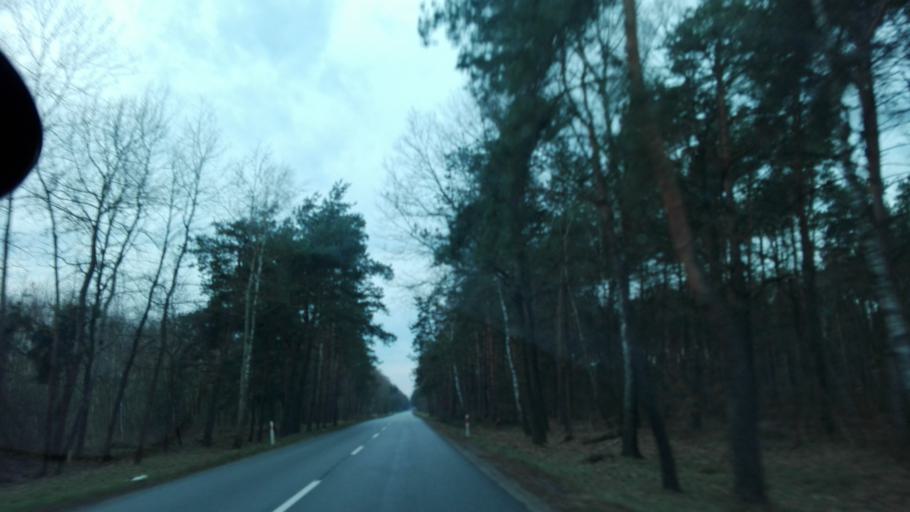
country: PL
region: Lublin Voivodeship
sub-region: Powiat radzynski
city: Wohyn
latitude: 51.7798
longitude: 22.7032
